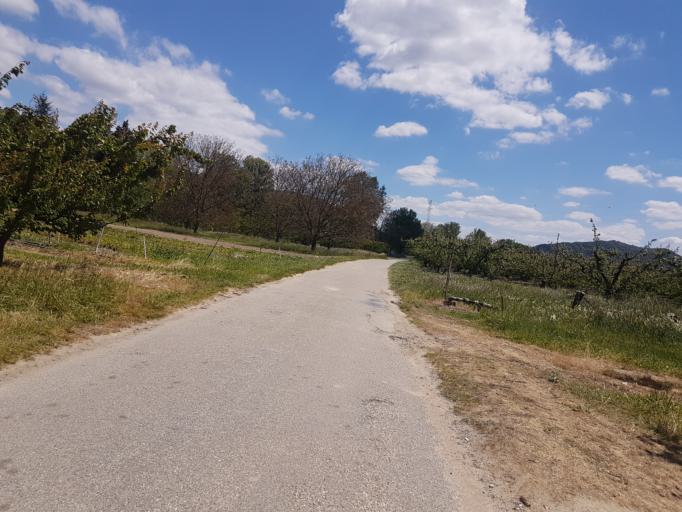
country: FR
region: Rhone-Alpes
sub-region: Departement de l'Ardeche
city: Saint-Jean-de-Muzols
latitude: 45.1090
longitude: 4.8137
